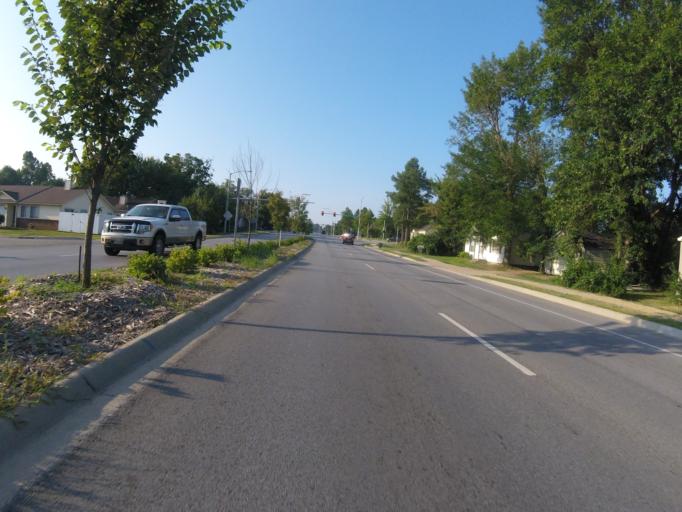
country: US
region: Arkansas
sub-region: Washington County
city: Fayetteville
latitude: 36.0865
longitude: -94.1751
